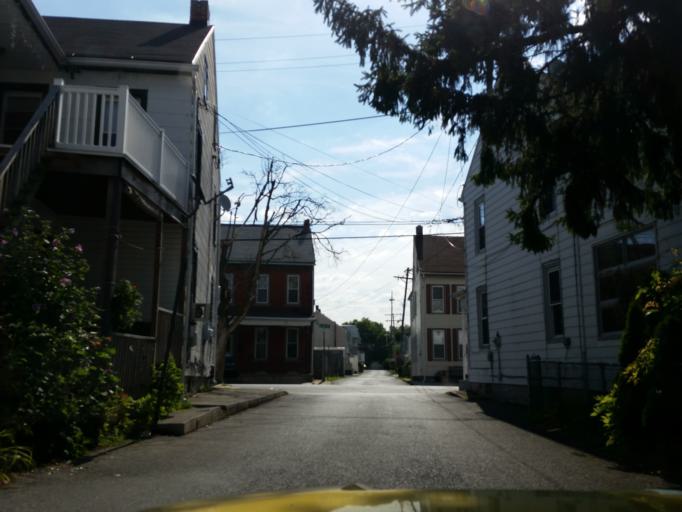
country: US
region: Pennsylvania
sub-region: Lebanon County
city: Lebanon
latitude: 40.3475
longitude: -76.4203
